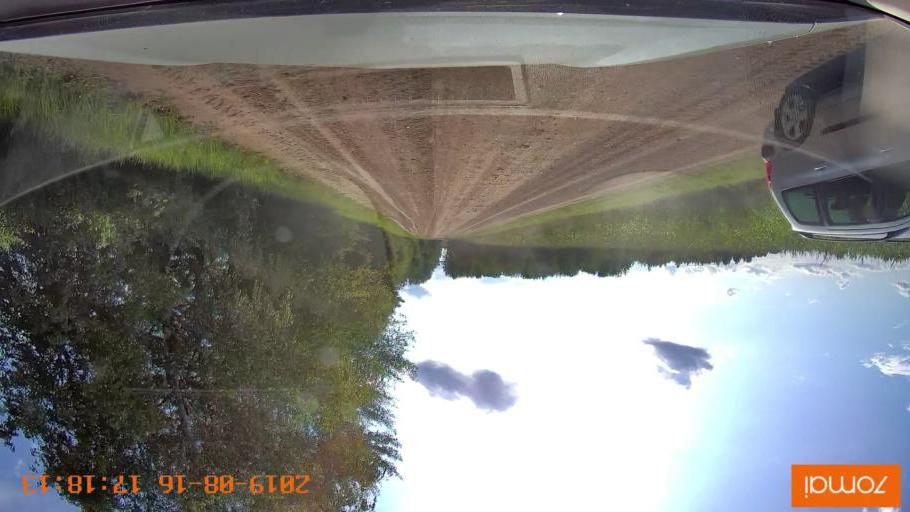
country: BY
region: Mogilev
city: Hlusha
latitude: 53.1699
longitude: 28.7932
